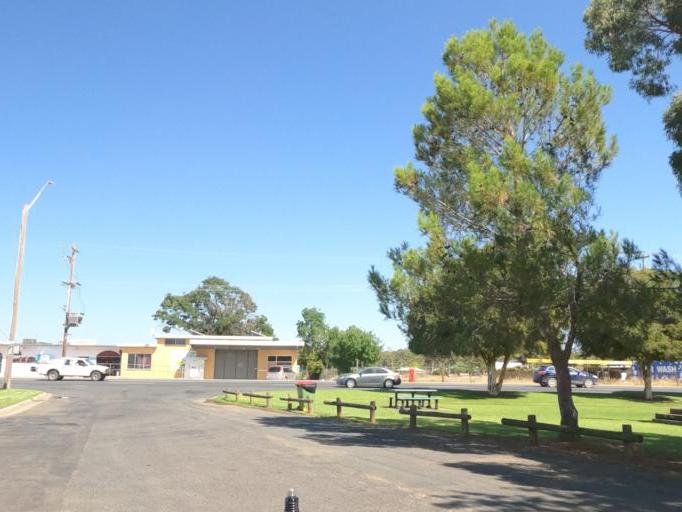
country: AU
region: New South Wales
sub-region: Corowa Shire
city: Mulwala
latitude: -35.9938
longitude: 146.0021
